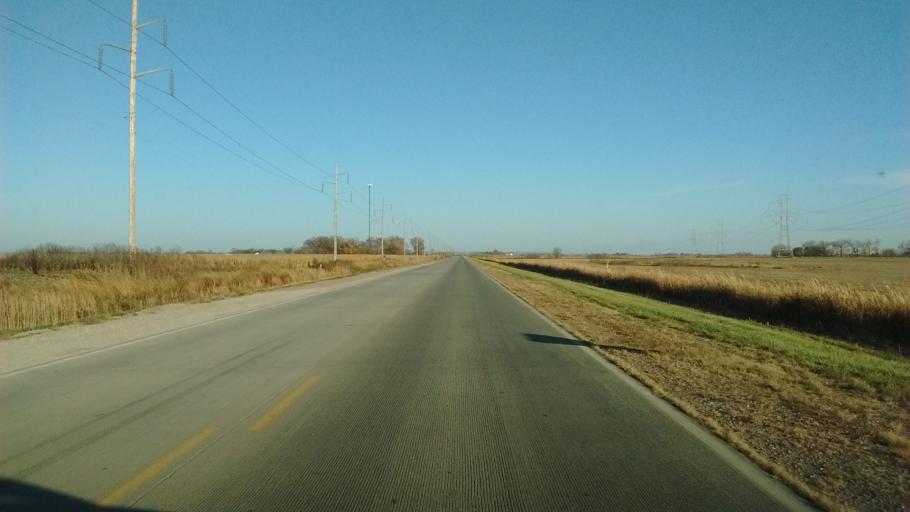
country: US
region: Iowa
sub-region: Woodbury County
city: Sergeant Bluff
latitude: 42.3302
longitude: -96.3459
